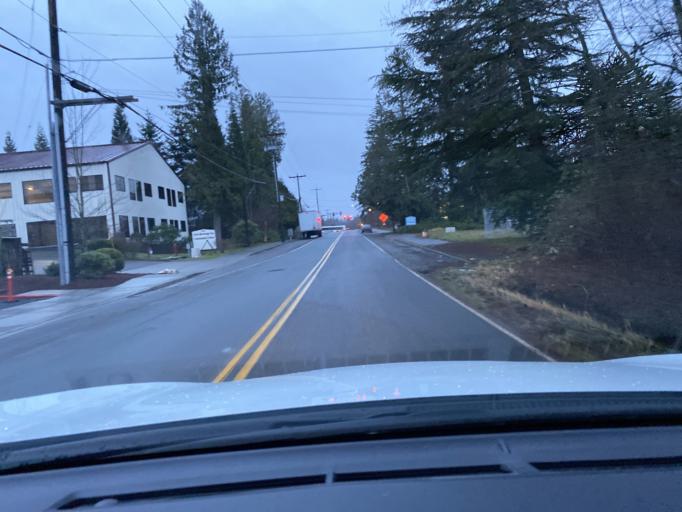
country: US
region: Washington
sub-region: Snohomish County
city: Mukilteo
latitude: 47.8906
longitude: -122.2894
